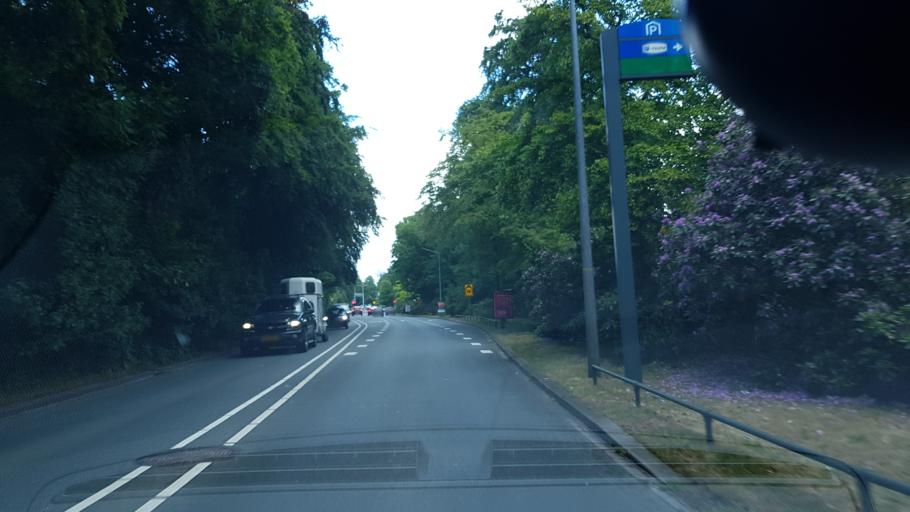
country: NL
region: North Holland
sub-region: Gemeente Hilversum
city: Hilversum
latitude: 52.2305
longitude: 5.1570
